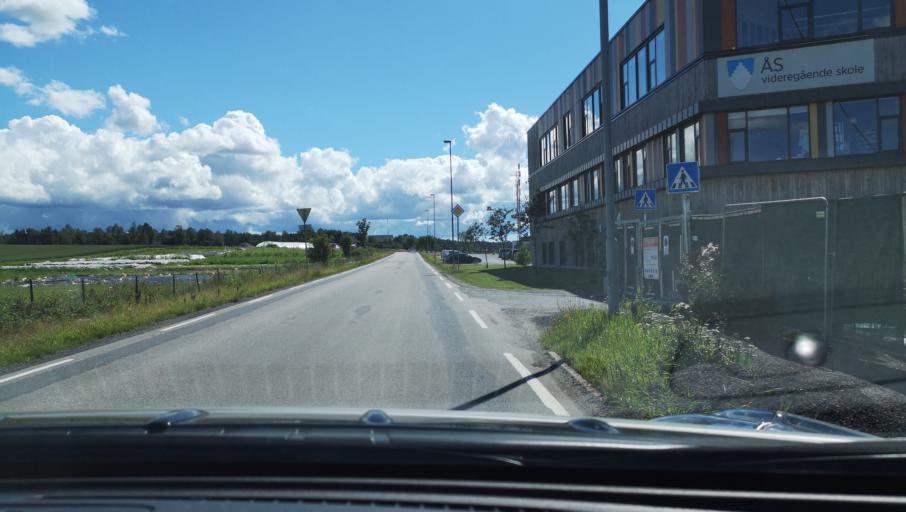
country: NO
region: Akershus
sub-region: As
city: As
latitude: 59.6641
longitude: 10.7980
